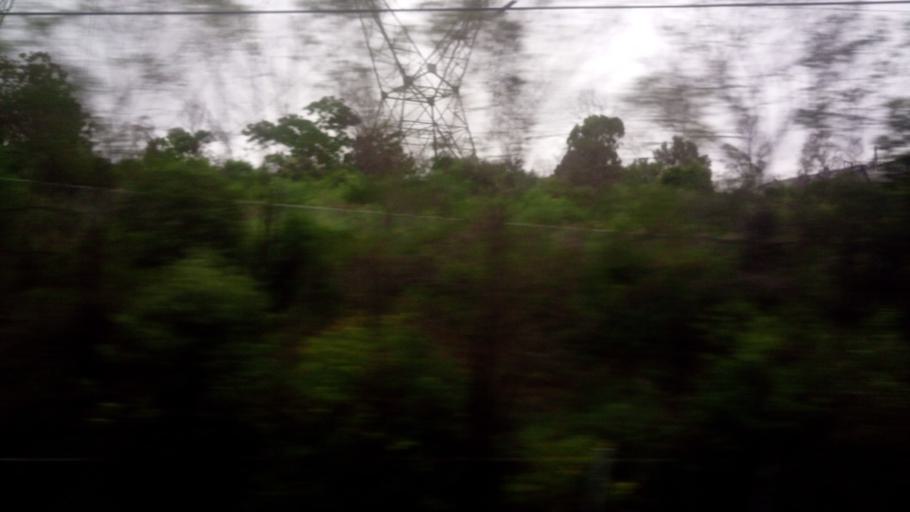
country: AU
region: New South Wales
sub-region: Blacktown
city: Mount Druitt
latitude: -33.7666
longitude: 150.8024
